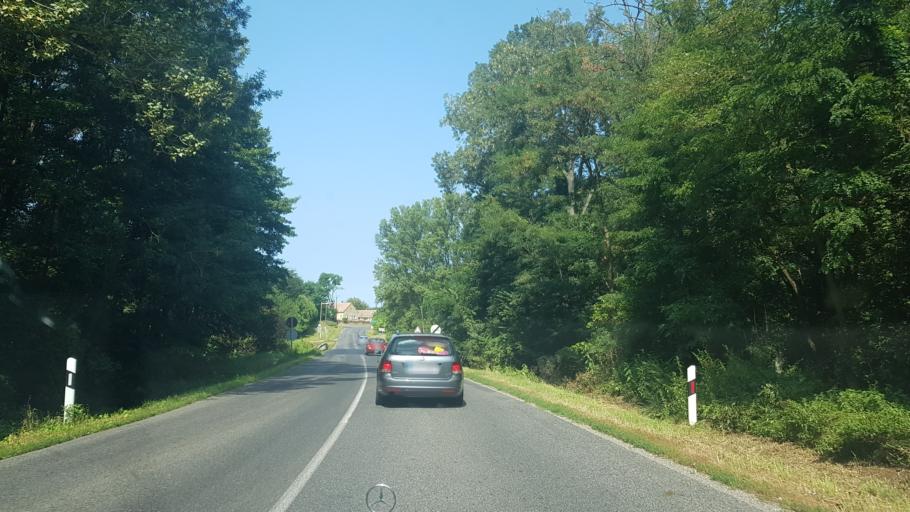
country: HU
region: Somogy
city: Marcali
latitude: 46.5195
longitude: 17.4243
